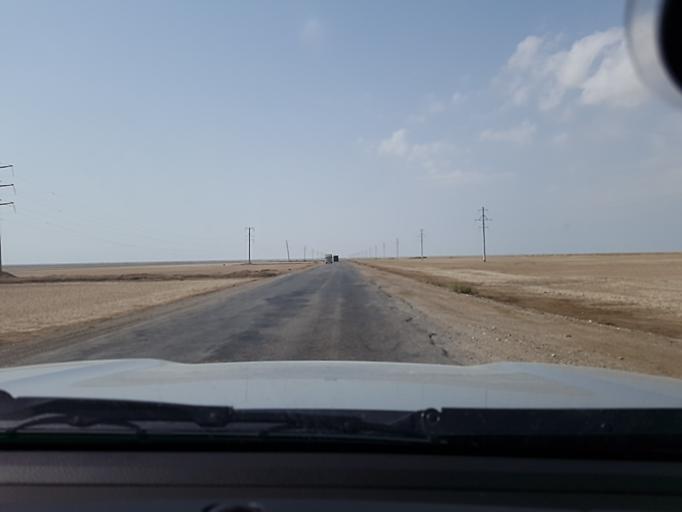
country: TM
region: Balkan
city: Gumdag
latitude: 39.0817
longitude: 54.5842
